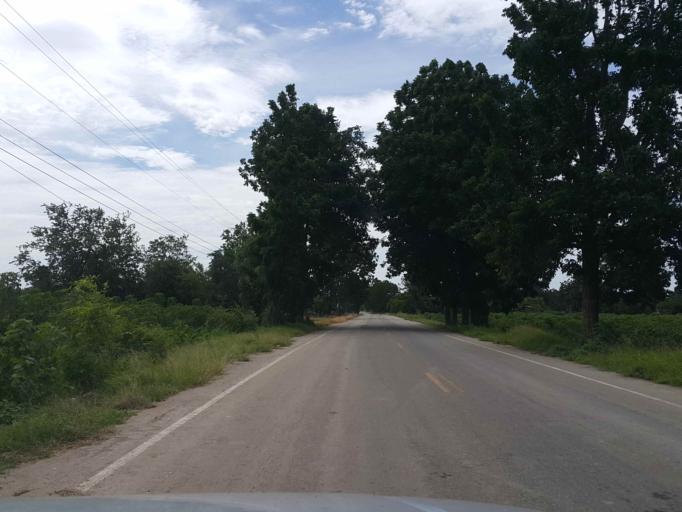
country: TH
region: Sukhothai
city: Ban Dan Lan Hoi
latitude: 17.0721
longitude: 99.4835
